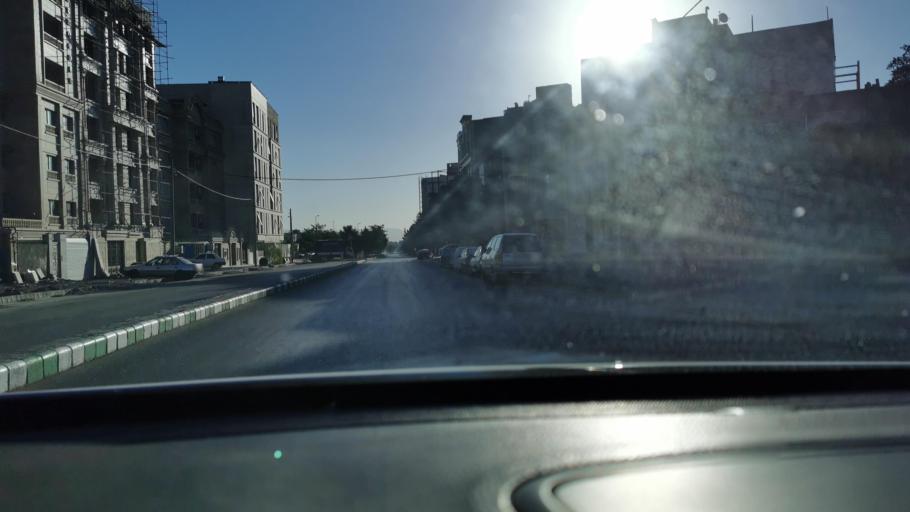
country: IR
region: Razavi Khorasan
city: Mashhad
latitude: 36.3610
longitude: 59.4844
